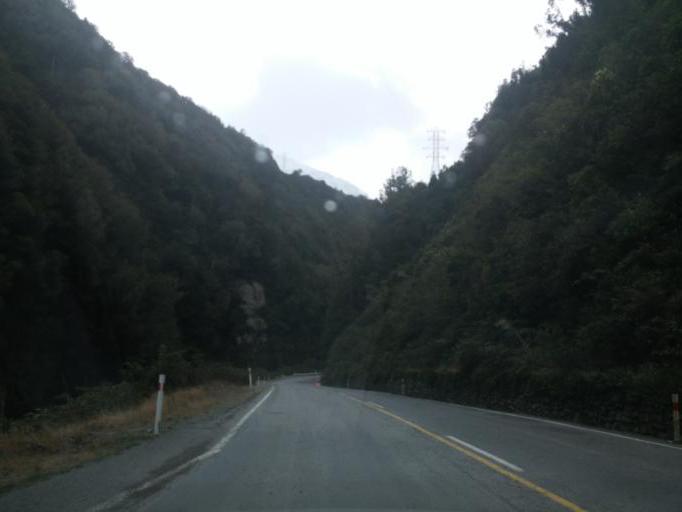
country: NZ
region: West Coast
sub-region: Grey District
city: Greymouth
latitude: -42.8730
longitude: 171.5553
